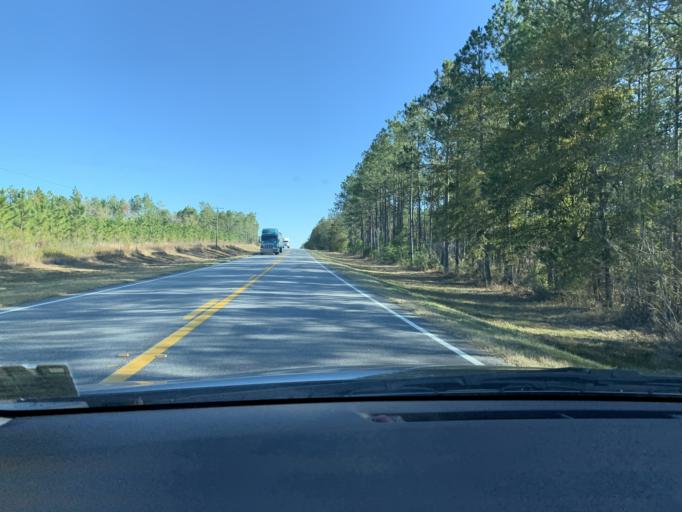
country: US
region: Georgia
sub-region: Ben Hill County
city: Fitzgerald
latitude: 31.7643
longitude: -83.1112
